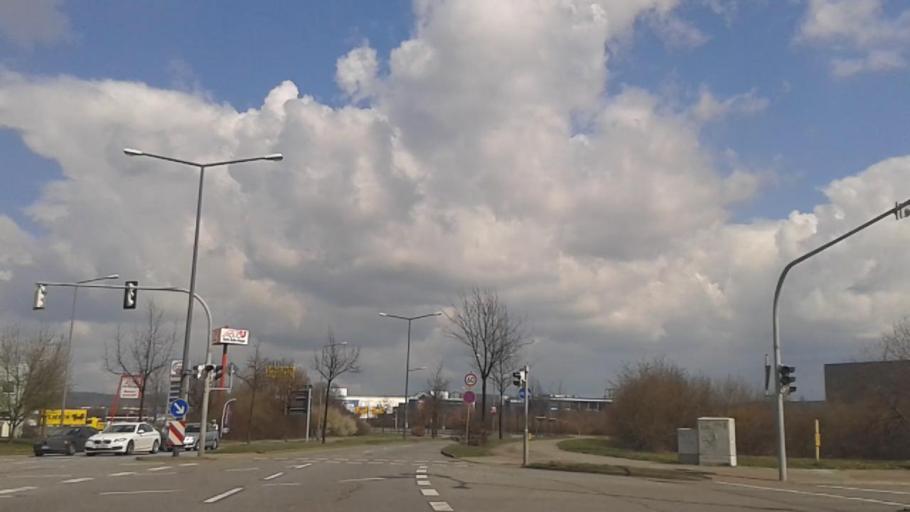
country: DE
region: Saxony
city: Radebeul
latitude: 51.0783
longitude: 13.6909
